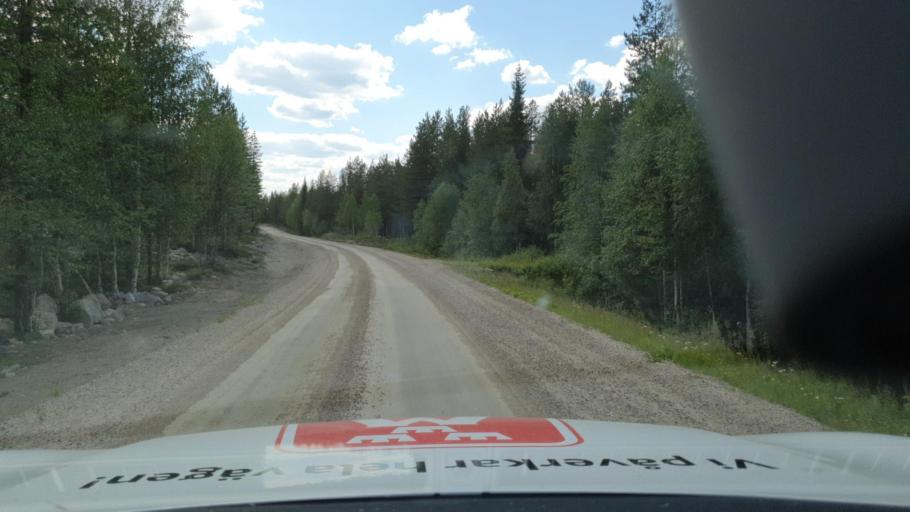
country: SE
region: Vaesterbotten
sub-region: Sorsele Kommun
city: Sorsele
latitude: 65.3519
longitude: 18.0013
